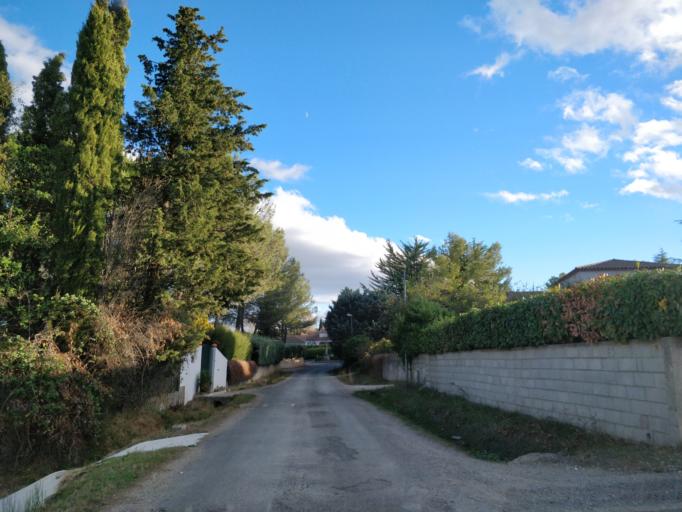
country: FR
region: Languedoc-Roussillon
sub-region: Departement de l'Herault
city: Beaulieu
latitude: 43.7465
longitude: 4.0014
